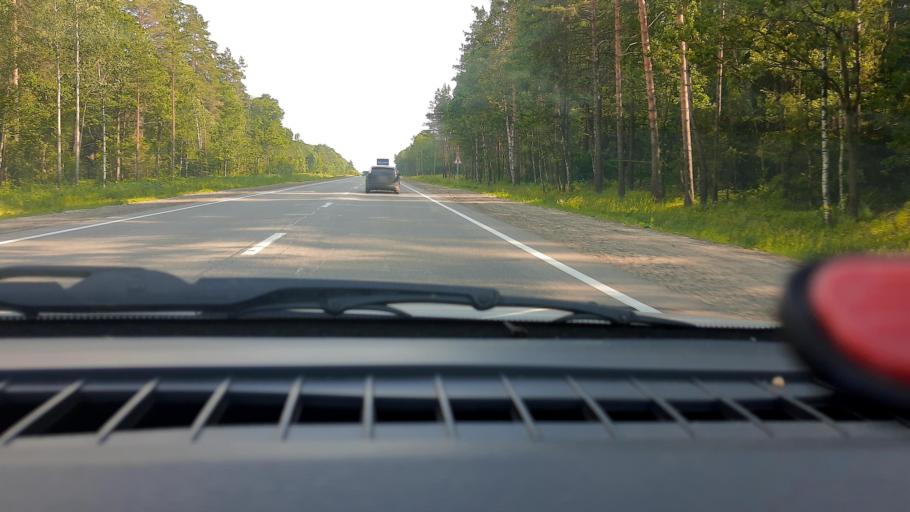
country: RU
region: Nizjnij Novgorod
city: Surovatikha
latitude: 55.7225
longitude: 43.9888
